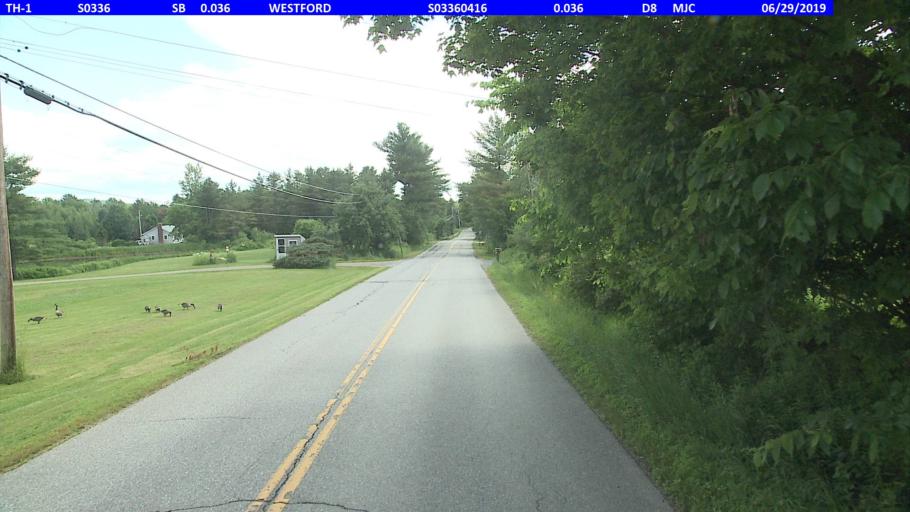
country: US
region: Vermont
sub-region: Chittenden County
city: Colchester
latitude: 44.5653
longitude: -73.0620
